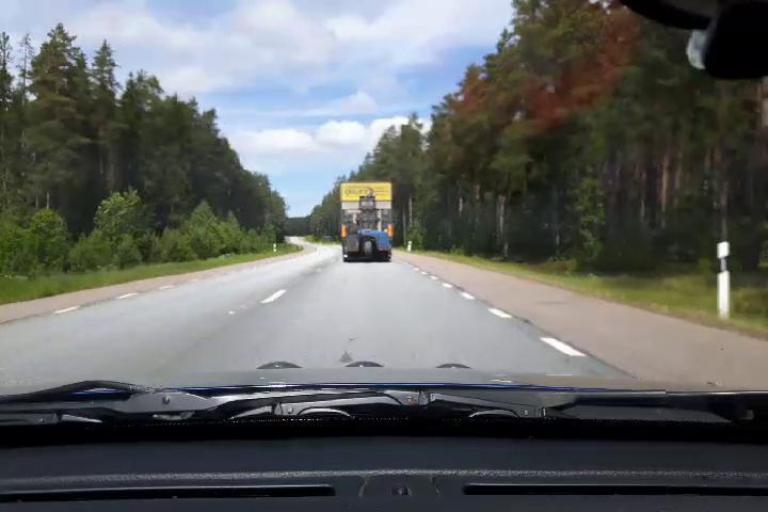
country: SE
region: Uppsala
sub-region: Tierps Kommun
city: Tierp
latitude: 60.1982
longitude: 17.4812
